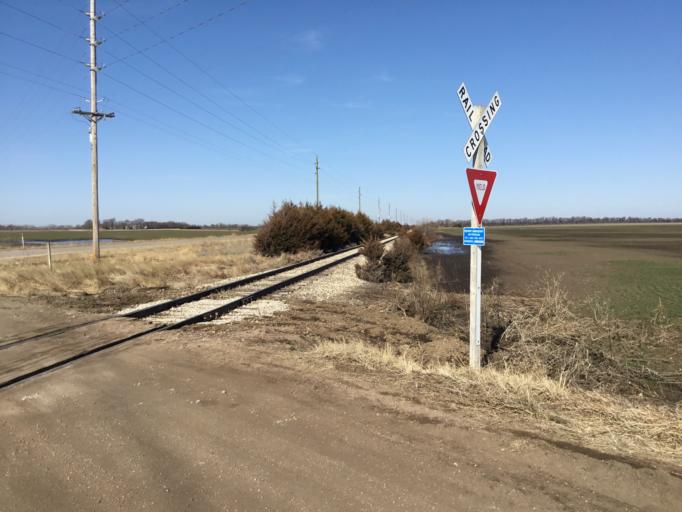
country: US
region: Kansas
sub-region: McPherson County
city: Moundridge
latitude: 38.2176
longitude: -97.5391
